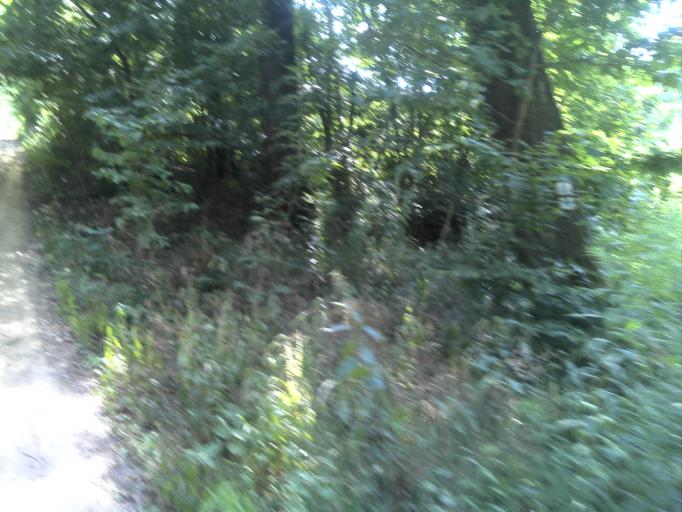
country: HU
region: Pest
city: Piliscsaba
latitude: 47.6462
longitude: 18.8519
